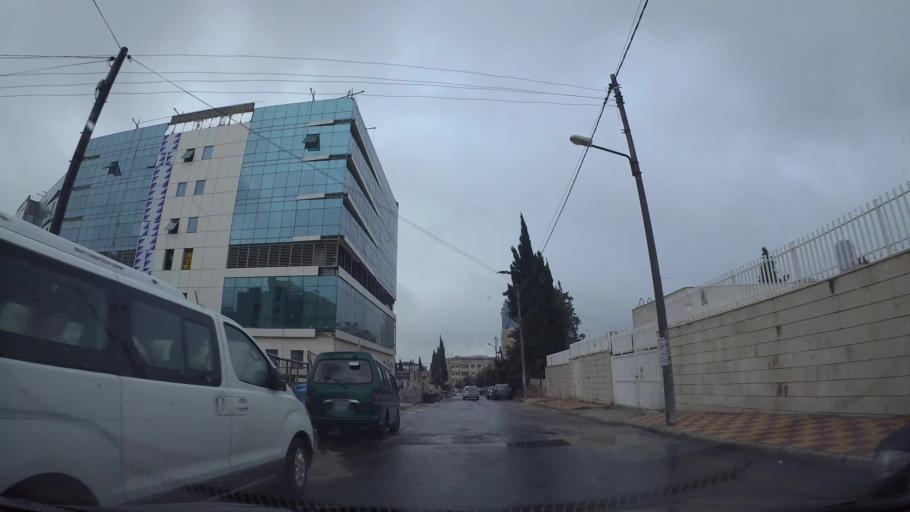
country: JO
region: Amman
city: Amman
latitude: 31.9696
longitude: 35.9115
